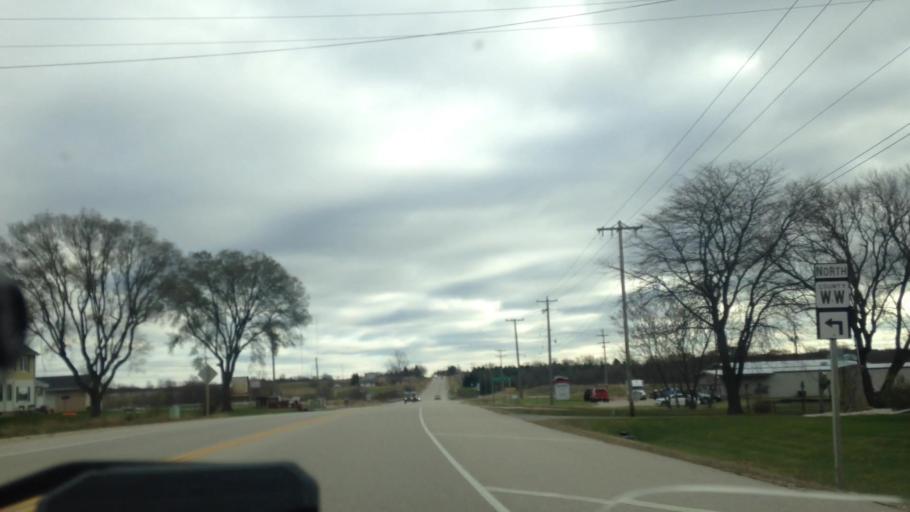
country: US
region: Wisconsin
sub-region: Washington County
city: Slinger
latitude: 43.4275
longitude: -88.3244
